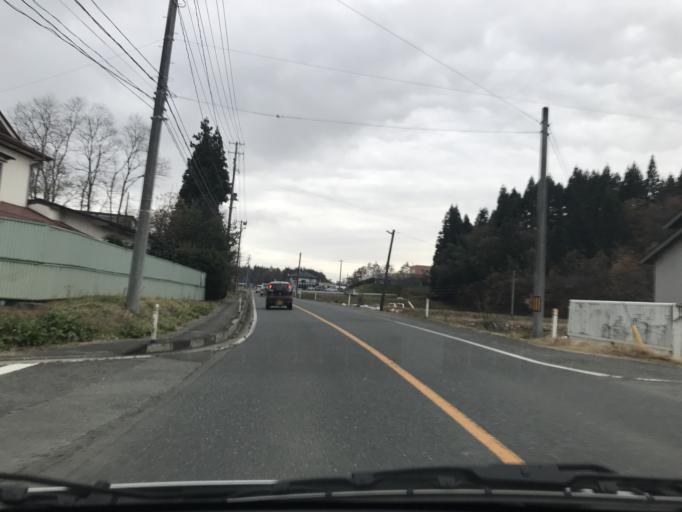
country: JP
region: Iwate
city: Ichinoseki
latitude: 39.0081
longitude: 141.3255
